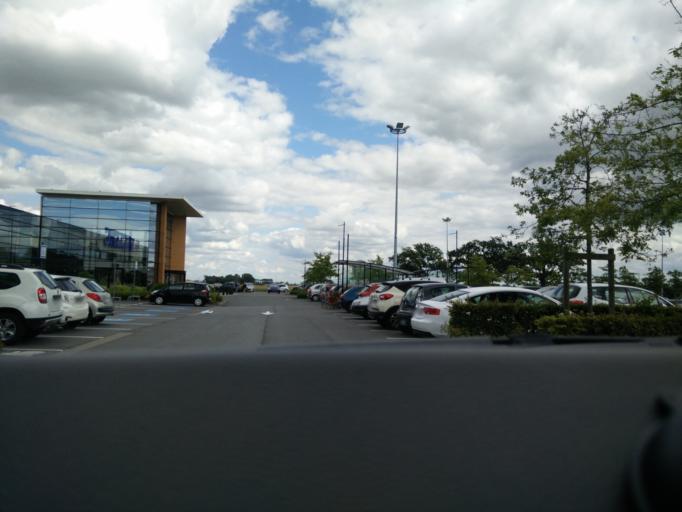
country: FR
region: Nord-Pas-de-Calais
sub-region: Departement du Nord
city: Bergues
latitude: 50.9571
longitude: 2.4348
